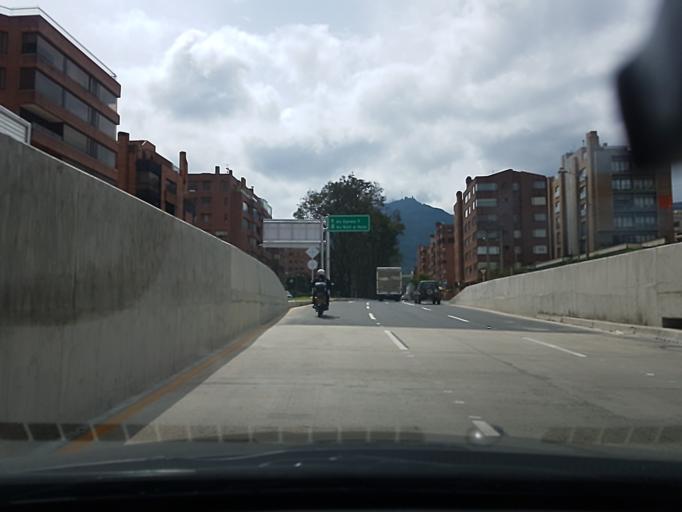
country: CO
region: Bogota D.C.
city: Barrio San Luis
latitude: 4.6809
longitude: -74.0534
